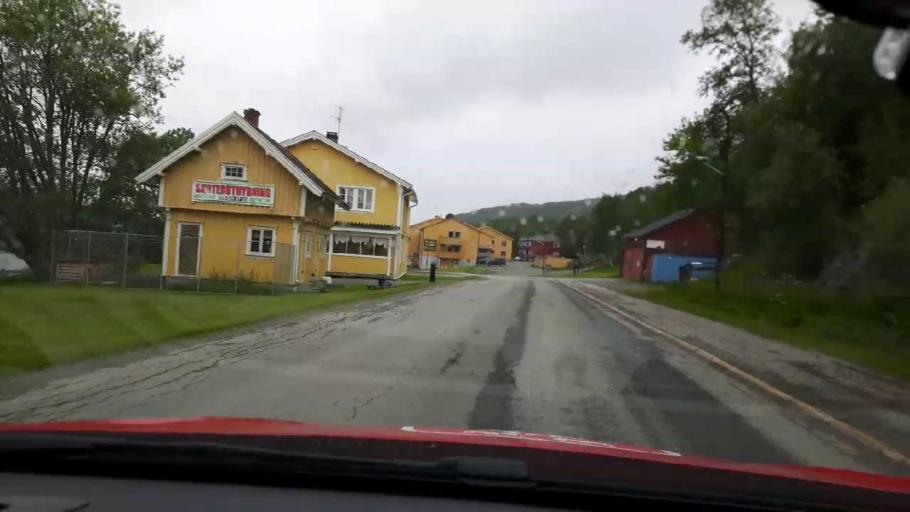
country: NO
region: Nord-Trondelag
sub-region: Meraker
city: Meraker
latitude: 63.3147
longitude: 12.1067
